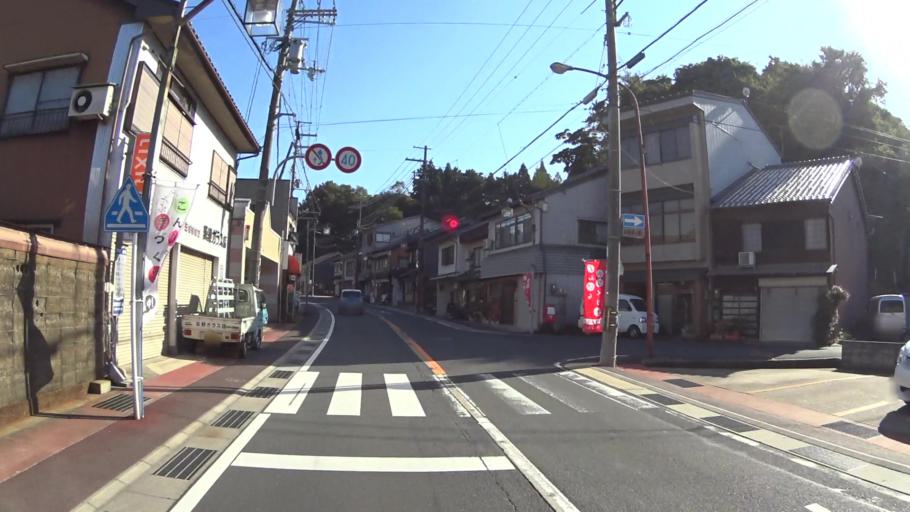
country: JP
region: Kyoto
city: Miyazu
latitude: 35.6217
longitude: 135.0596
